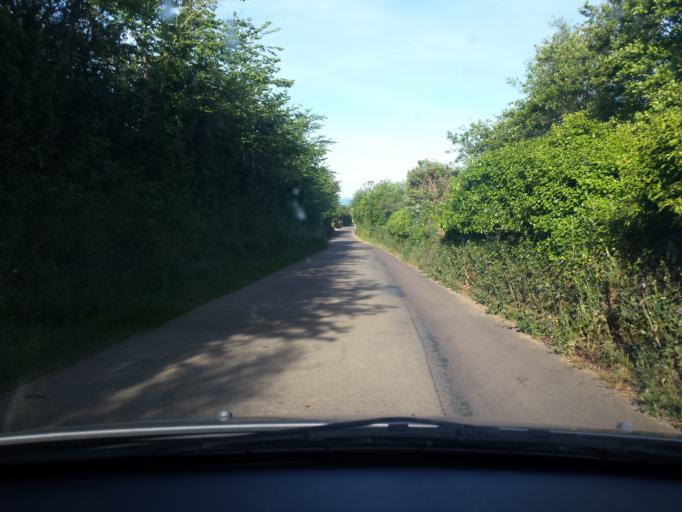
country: FR
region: Lower Normandy
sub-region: Departement de la Manche
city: Beaumont-Hague
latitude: 49.6780
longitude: -1.9133
